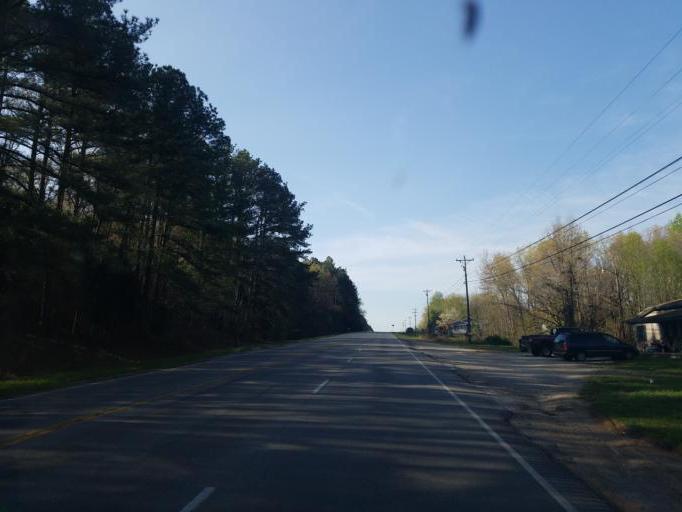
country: US
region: Kentucky
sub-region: Hart County
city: Munfordville
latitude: 37.3270
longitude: -85.9091
